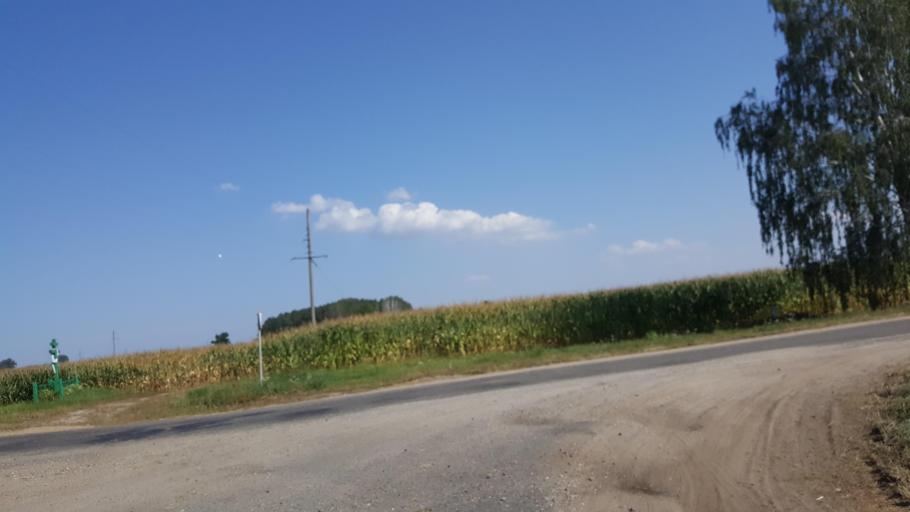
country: PL
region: Podlasie
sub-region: Powiat hajnowski
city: Czeremcha
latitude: 52.4870
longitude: 23.5475
